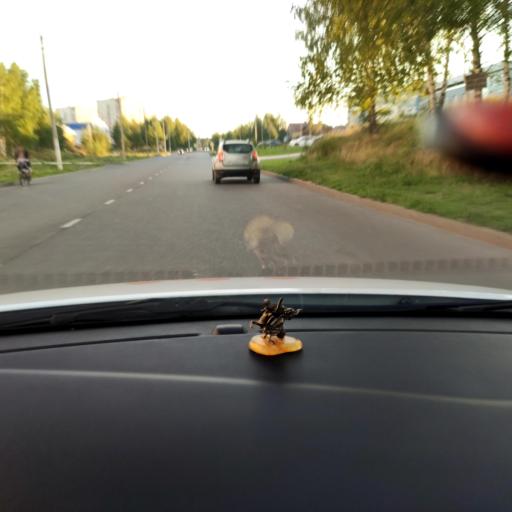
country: RU
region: Tatarstan
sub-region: Zelenodol'skiy Rayon
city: Zelenodolsk
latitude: 55.8666
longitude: 48.5639
